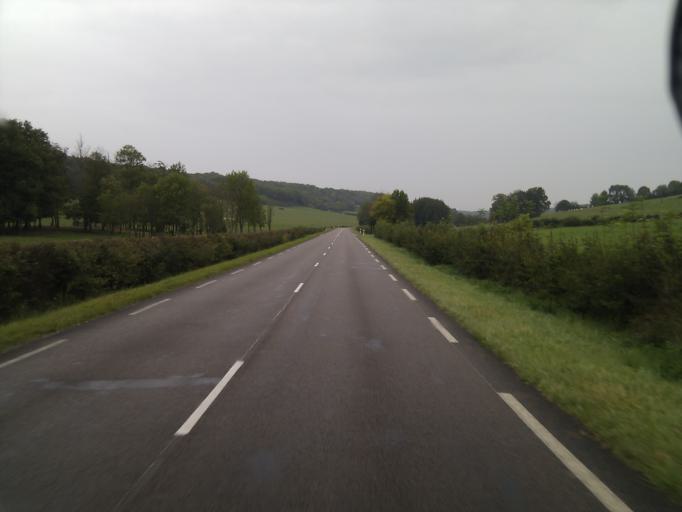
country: FR
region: Bourgogne
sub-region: Departement de la Cote-d'Or
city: Montbard
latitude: 47.5688
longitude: 4.3365
